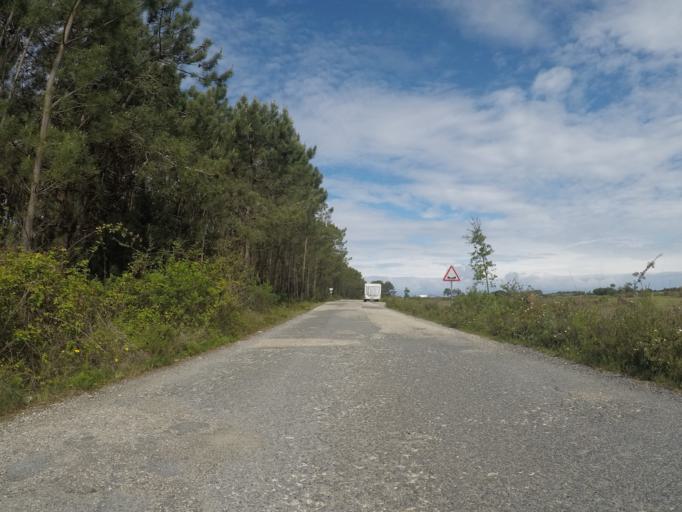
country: PT
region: Beja
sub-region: Odemira
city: Sao Teotonio
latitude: 37.4472
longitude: -8.7622
